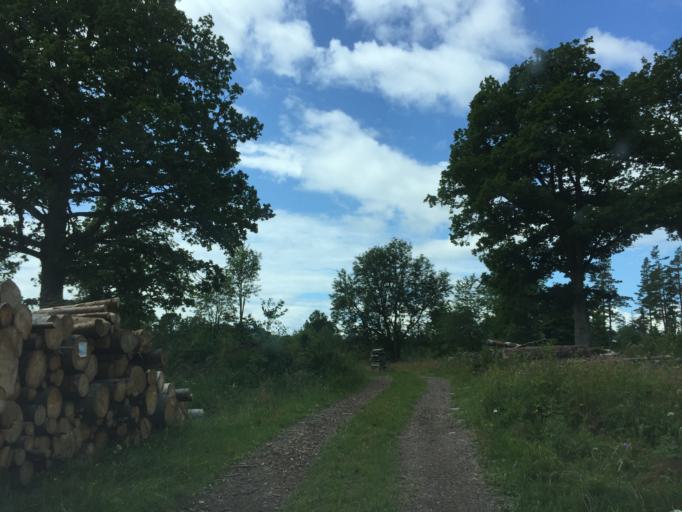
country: SE
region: OEstergoetland
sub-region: Odeshogs Kommun
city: OEdeshoeg
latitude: 58.1760
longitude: 14.6904
